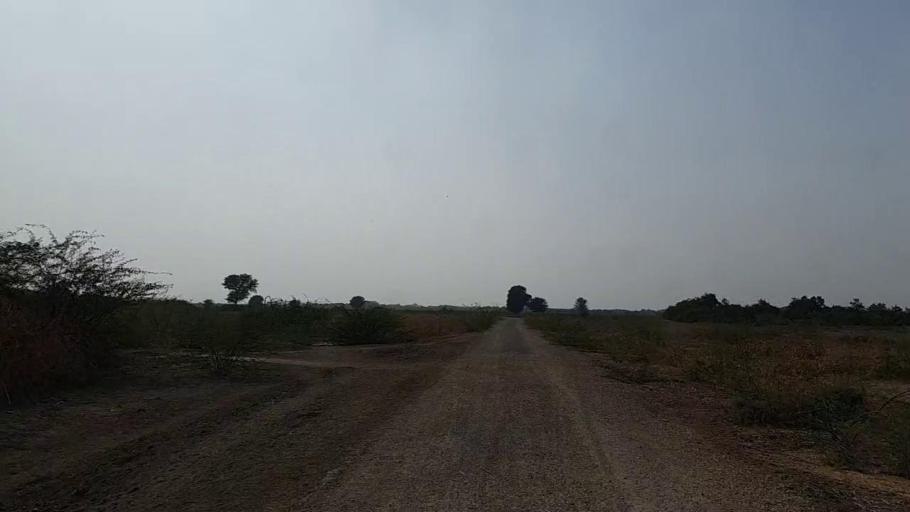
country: PK
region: Sindh
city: Naukot
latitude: 24.7577
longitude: 69.3129
